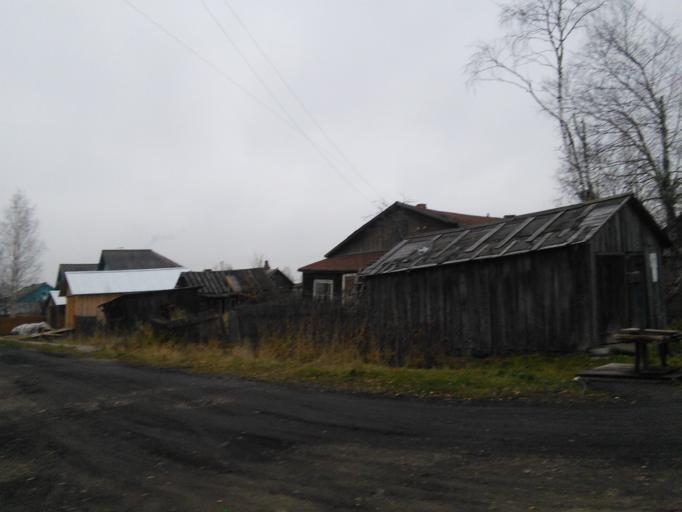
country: RU
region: Vologda
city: Kharovsk
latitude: 59.8088
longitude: 40.1740
